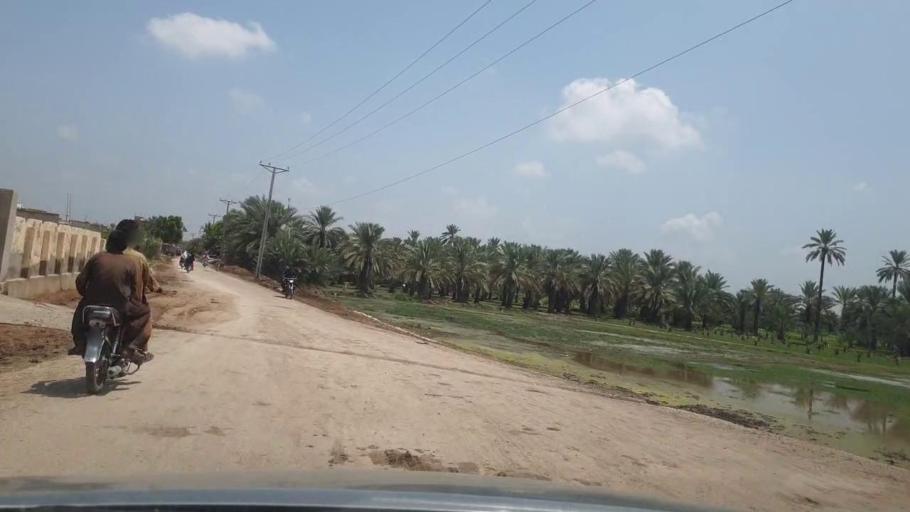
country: PK
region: Sindh
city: Pir jo Goth
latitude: 27.6002
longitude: 68.6035
